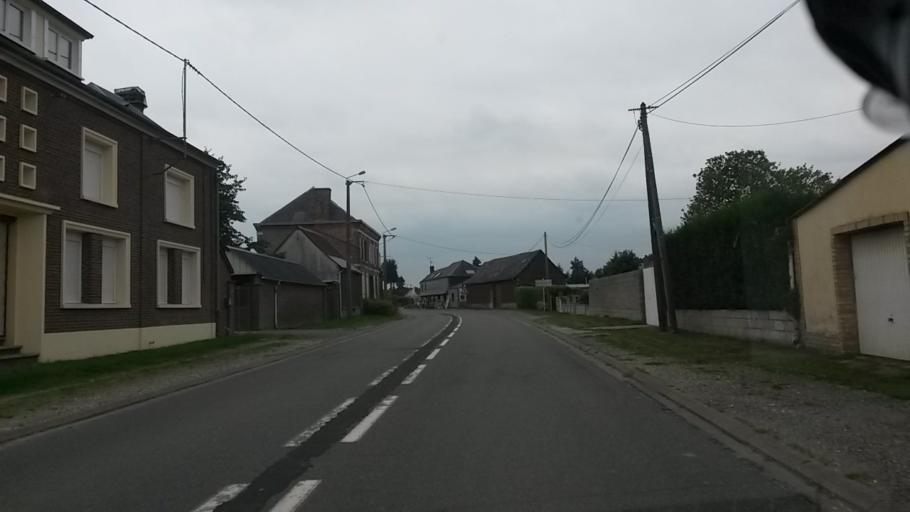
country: FR
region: Picardie
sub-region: Departement de la Somme
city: Hornoy-le-Bourg
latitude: 49.7796
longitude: 1.8908
